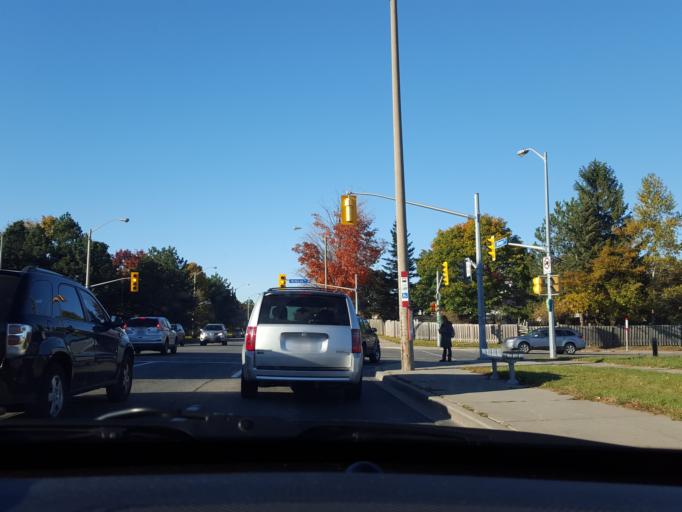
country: CA
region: Ontario
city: Scarborough
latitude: 43.8153
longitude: -79.2816
